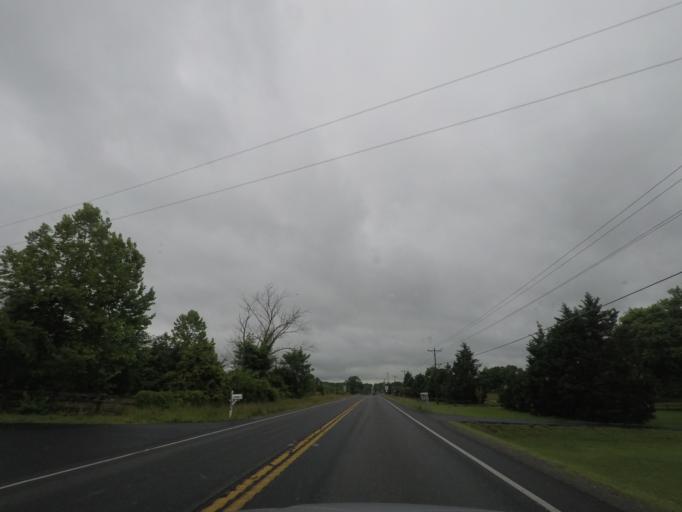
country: US
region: Virginia
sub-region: Prince William County
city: Bull Run Mountain Estates
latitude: 38.8828
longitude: -77.6333
